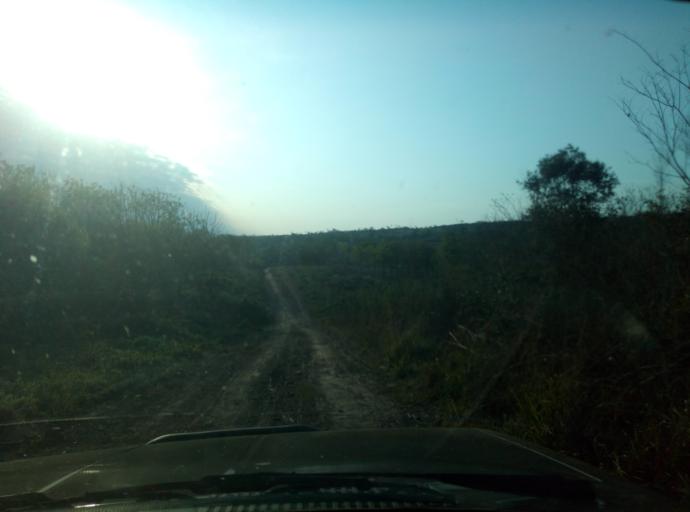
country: PY
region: Caaguazu
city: San Joaquin
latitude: -25.1990
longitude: -56.1168
